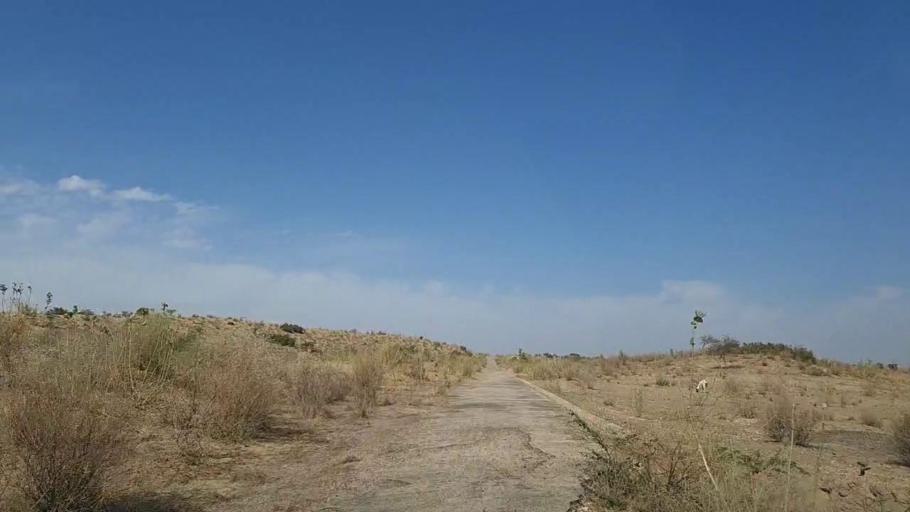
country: PK
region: Sindh
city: Nabisar
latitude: 24.8762
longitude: 69.6114
